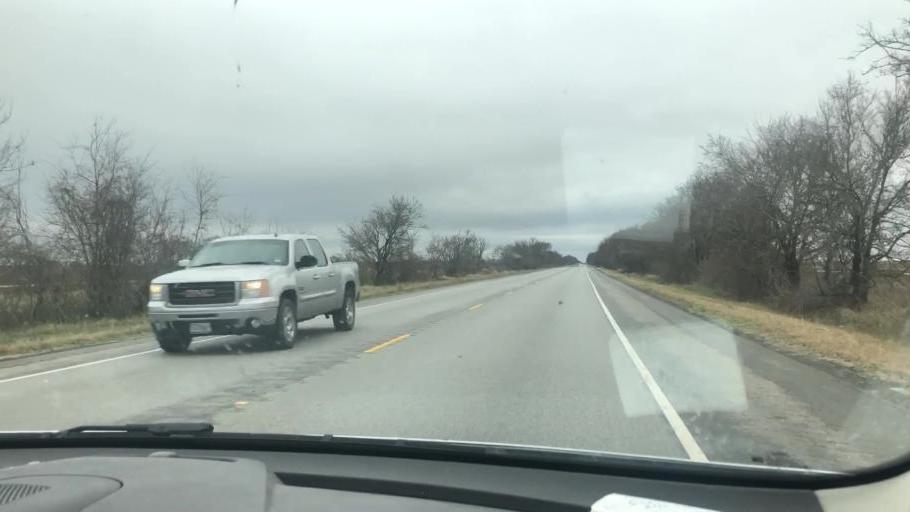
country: US
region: Texas
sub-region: Matagorda County
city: Van Vleck
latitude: 29.1187
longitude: -95.9806
